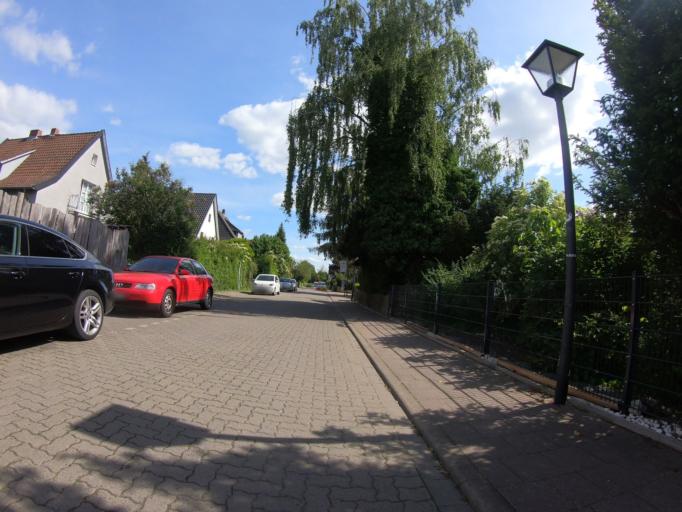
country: DE
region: Lower Saxony
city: Wolfenbuettel
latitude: 52.1737
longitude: 10.5376
